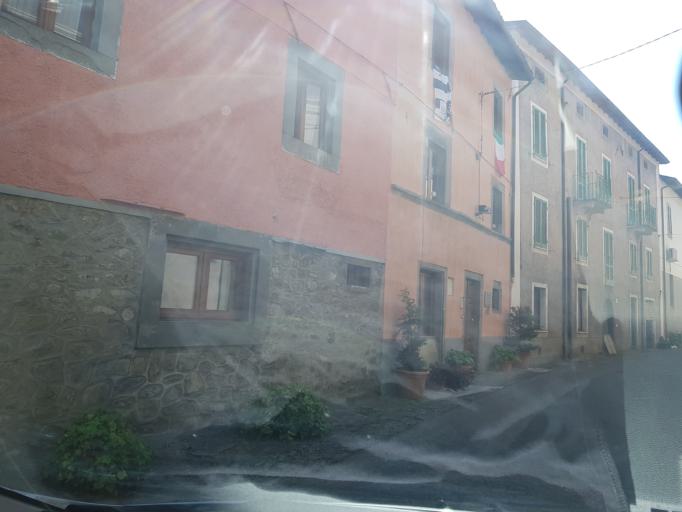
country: IT
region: Tuscany
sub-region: Provincia di Lucca
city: Camporgiano
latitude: 44.1590
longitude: 10.3350
